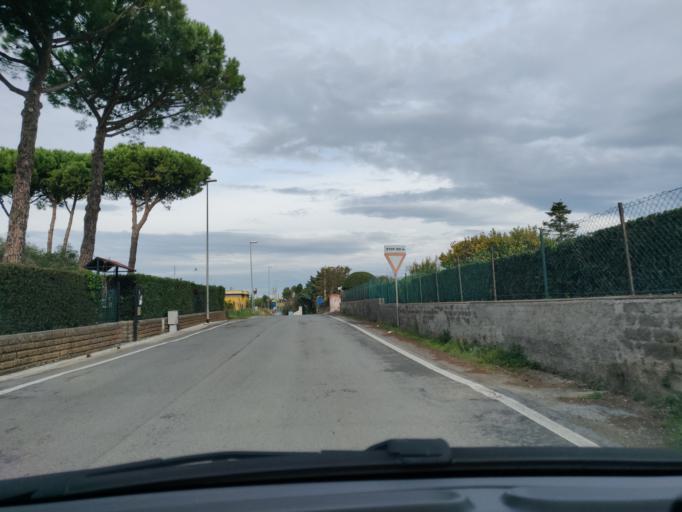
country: IT
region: Latium
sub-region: Citta metropolitana di Roma Capitale
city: Civitavecchia
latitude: 42.1032
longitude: 11.8123
